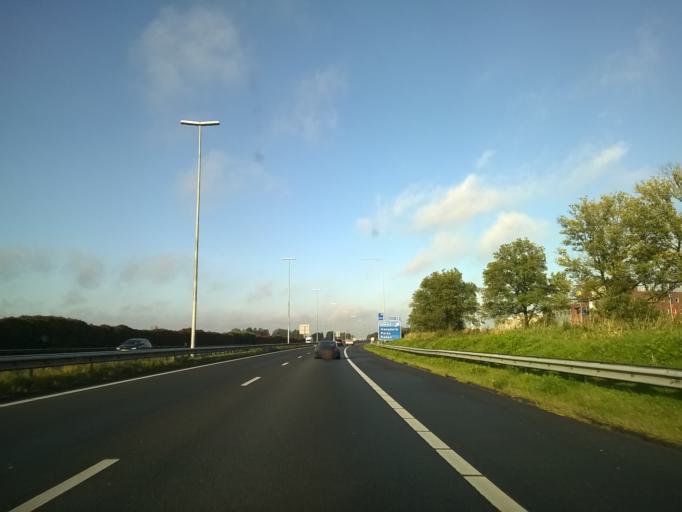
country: NL
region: Groningen
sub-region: Gemeente Groningen
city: Groningen
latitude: 53.1959
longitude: 6.5304
